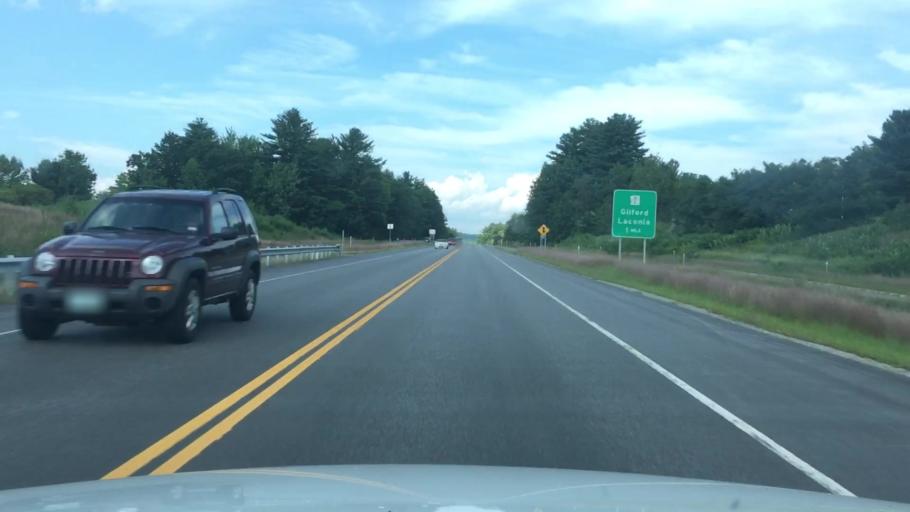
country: US
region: New Hampshire
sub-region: Belknap County
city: Laconia
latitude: 43.5149
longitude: -71.4526
